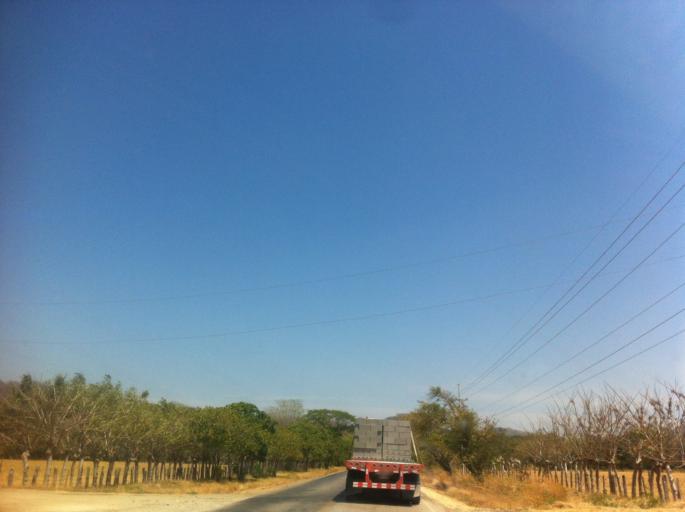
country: CR
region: Guanacaste
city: Santa Cruz
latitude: 10.2303
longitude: -85.5478
